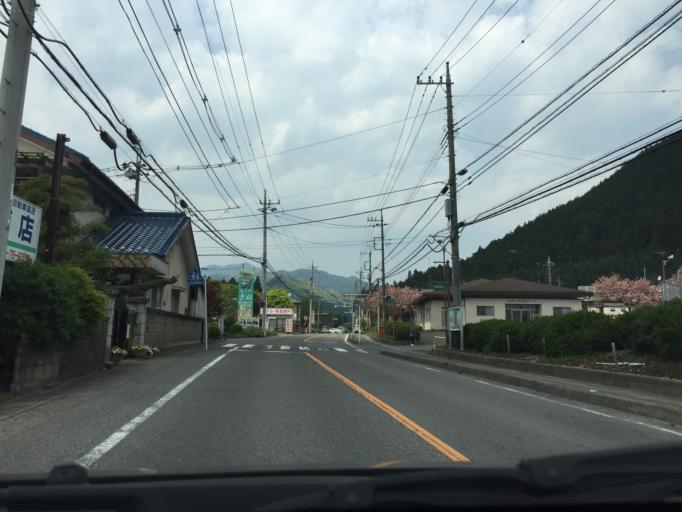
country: JP
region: Tochigi
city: Imaichi
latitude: 36.7867
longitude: 139.7074
